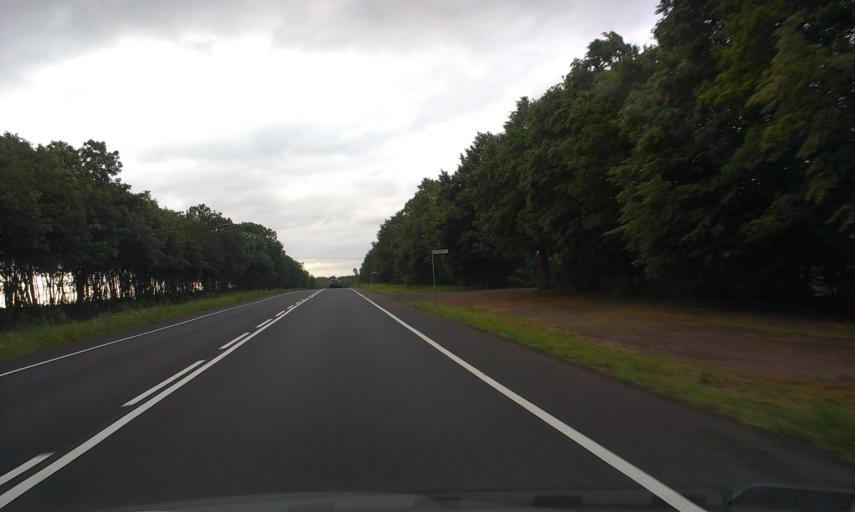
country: PL
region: Greater Poland Voivodeship
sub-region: Powiat pilski
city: Ujscie
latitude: 53.0365
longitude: 16.7742
